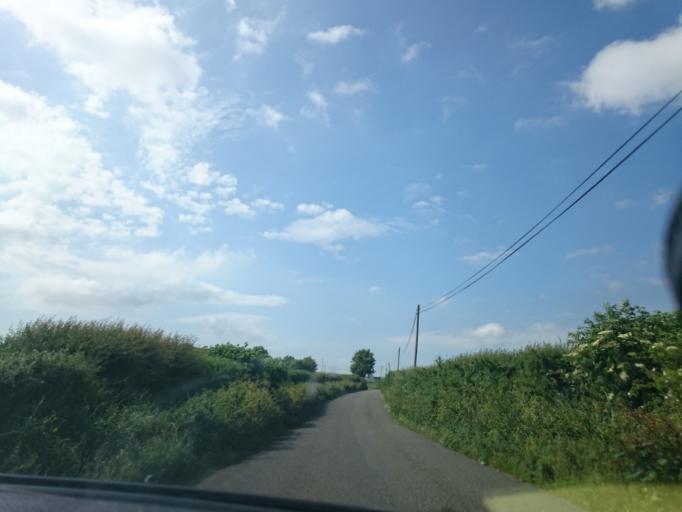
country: IE
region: Leinster
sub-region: Kilkenny
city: Thomastown
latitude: 52.5228
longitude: -7.1990
